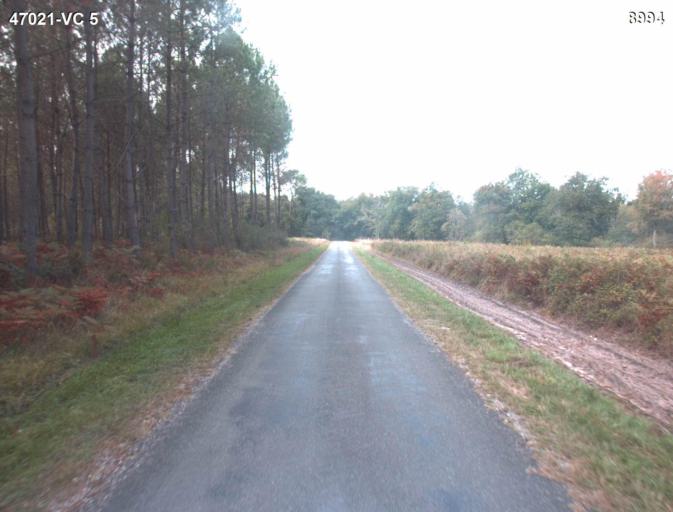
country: FR
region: Aquitaine
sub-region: Departement du Lot-et-Garonne
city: Barbaste
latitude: 44.1572
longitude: 0.1910
